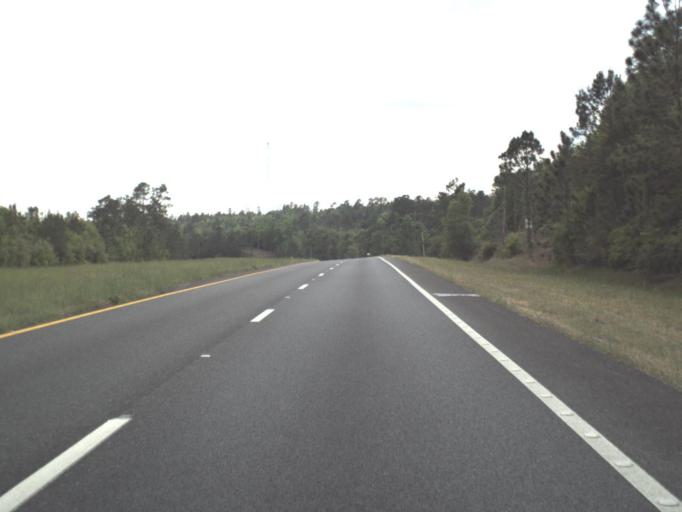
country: US
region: Florida
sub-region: Escambia County
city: Century
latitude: 30.9009
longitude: -87.3183
